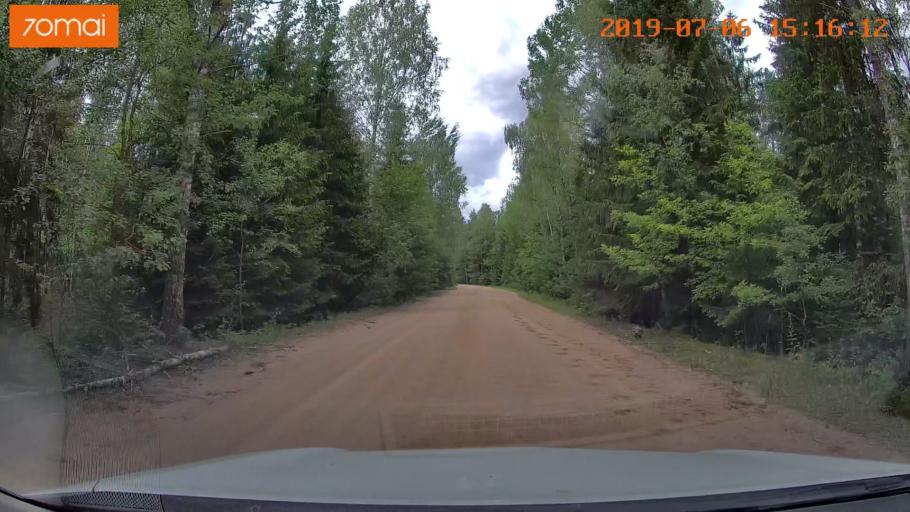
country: BY
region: Minsk
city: Ivyanyets
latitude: 53.9792
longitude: 26.6805
